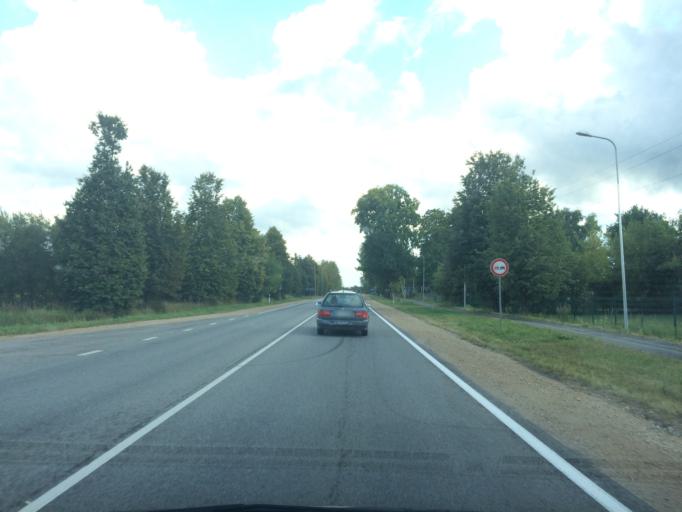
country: LV
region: Ogre
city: Ogre
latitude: 56.7805
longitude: 24.6518
